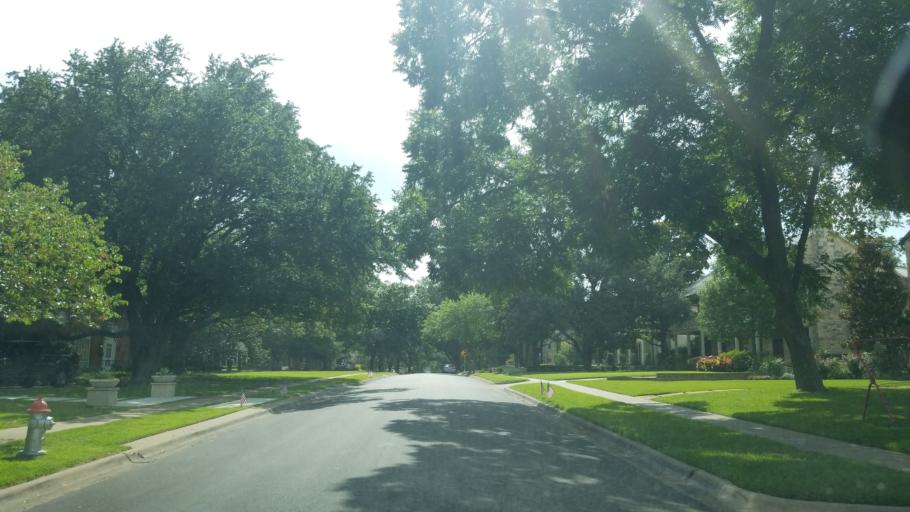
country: US
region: Texas
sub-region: Dallas County
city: University Park
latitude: 32.8634
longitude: -96.7902
